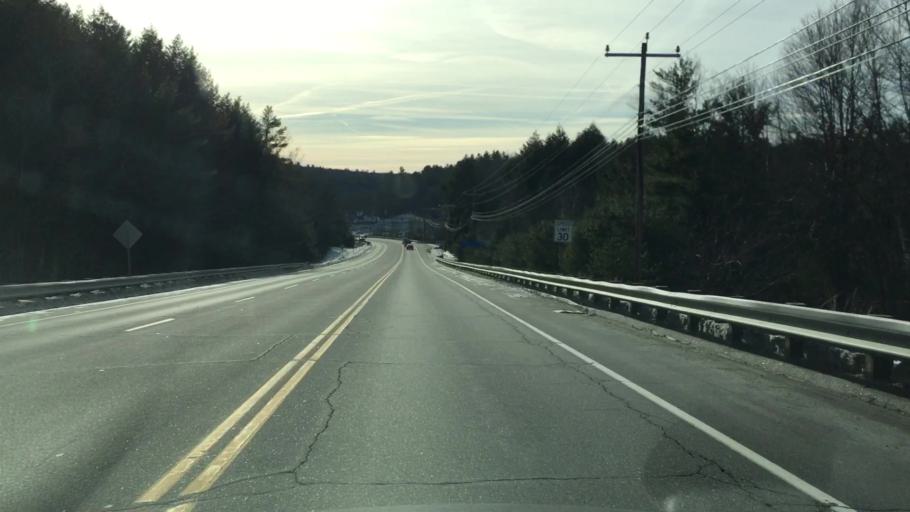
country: US
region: New Hampshire
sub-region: Sullivan County
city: Sunapee
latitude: 43.3954
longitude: -72.0851
